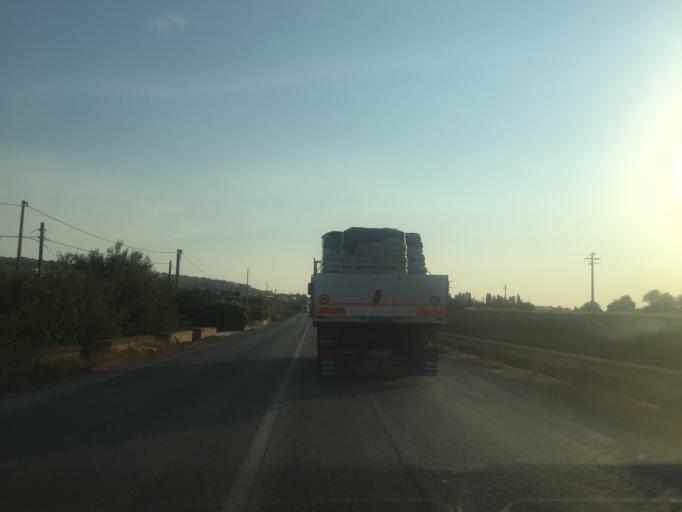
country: IT
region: Sicily
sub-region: Ragusa
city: Ispica
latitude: 36.7650
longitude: 14.8999
